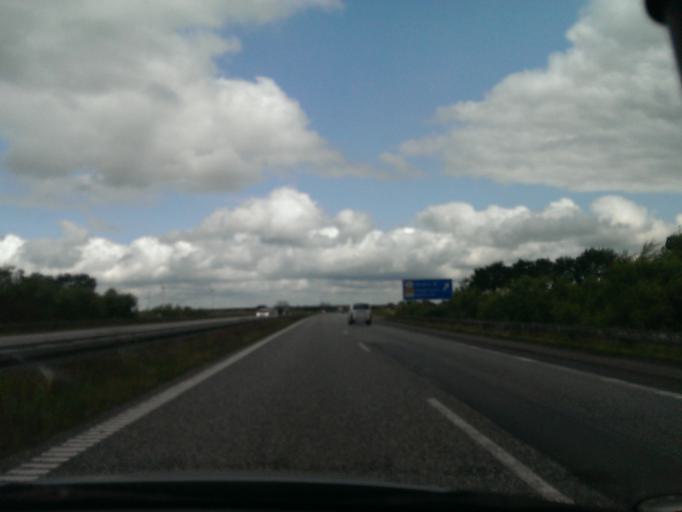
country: DK
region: North Denmark
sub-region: Mariagerfjord Kommune
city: Hobro
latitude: 56.6619
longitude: 9.7351
